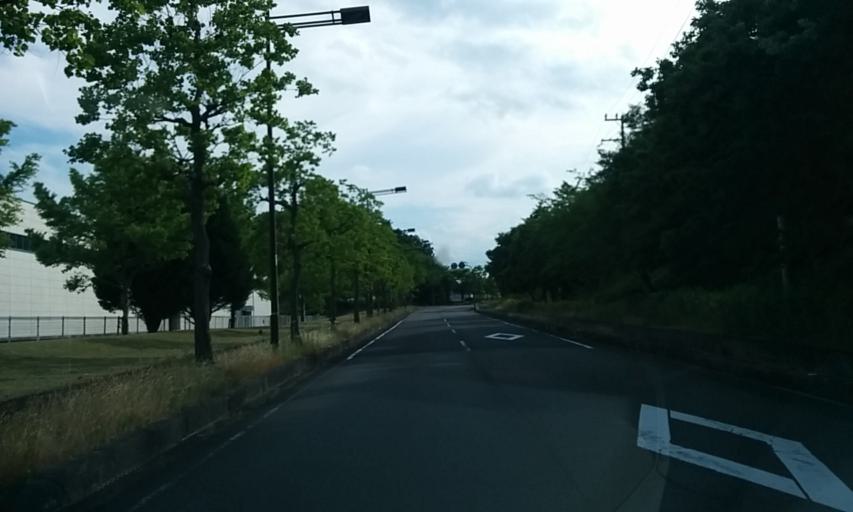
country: JP
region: Kyoto
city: Ayabe
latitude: 35.3300
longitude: 135.2861
